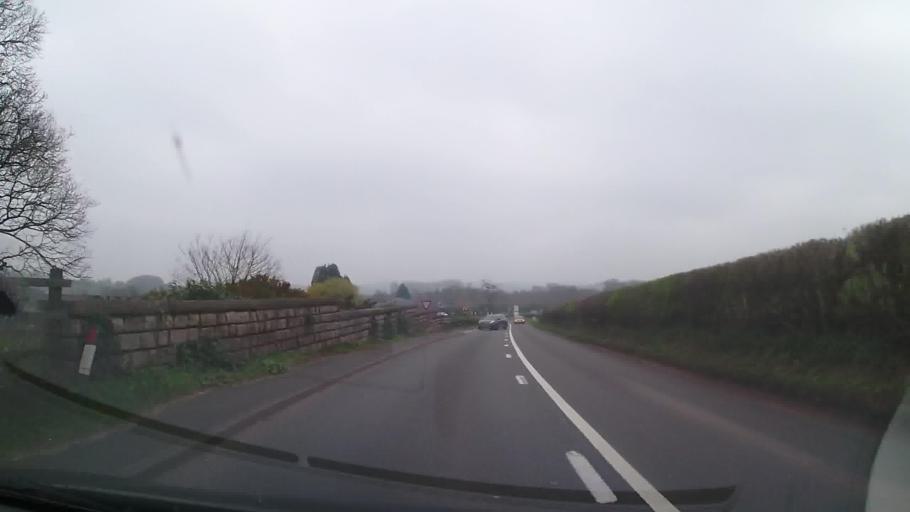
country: GB
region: England
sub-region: Staffordshire
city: Standon
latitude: 52.9563
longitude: -2.3145
